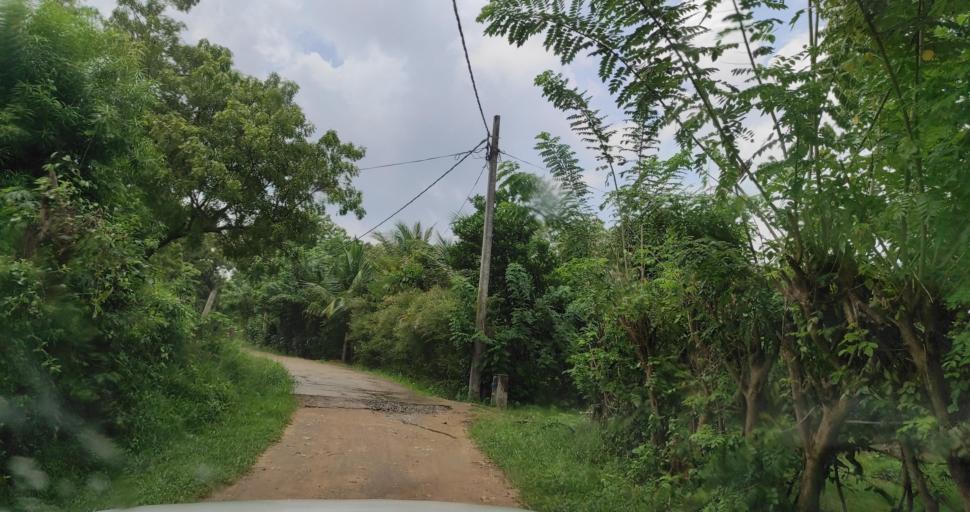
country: LK
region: Eastern Province
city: Trincomalee
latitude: 8.3709
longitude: 81.0145
